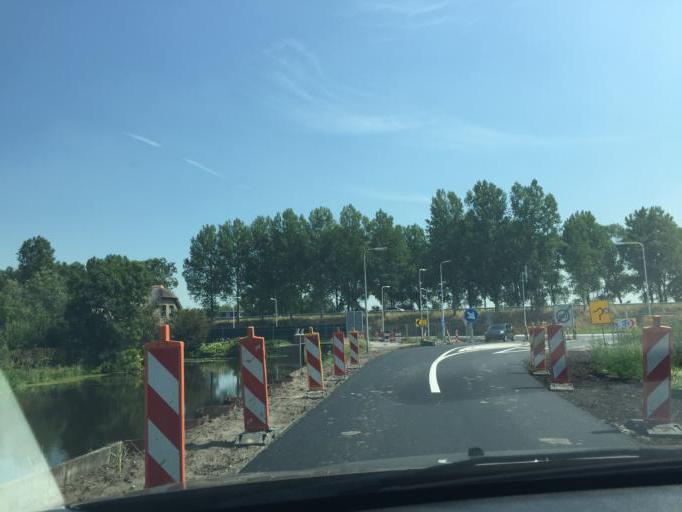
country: NL
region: South Holland
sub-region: Bodegraven-Reeuwijk
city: Reeuwijk
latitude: 52.0547
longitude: 4.7203
